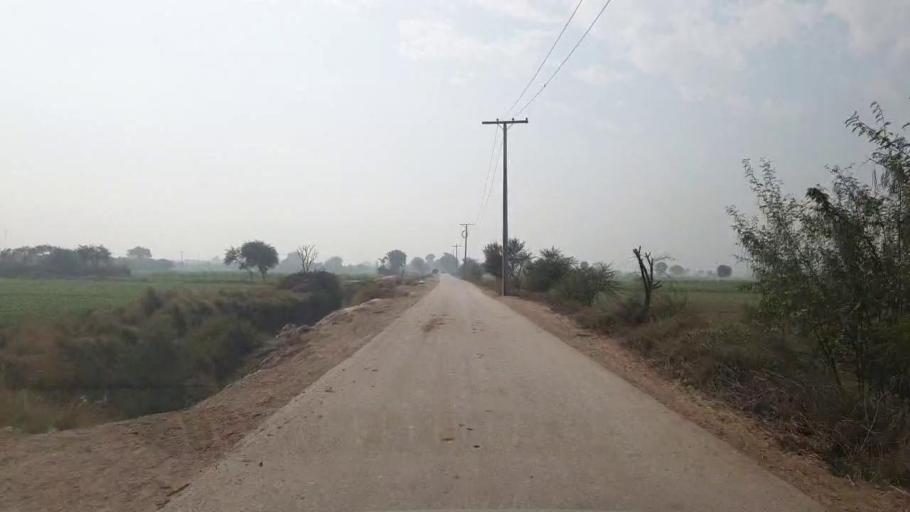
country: PK
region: Sindh
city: Hala
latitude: 25.7570
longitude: 68.4464
